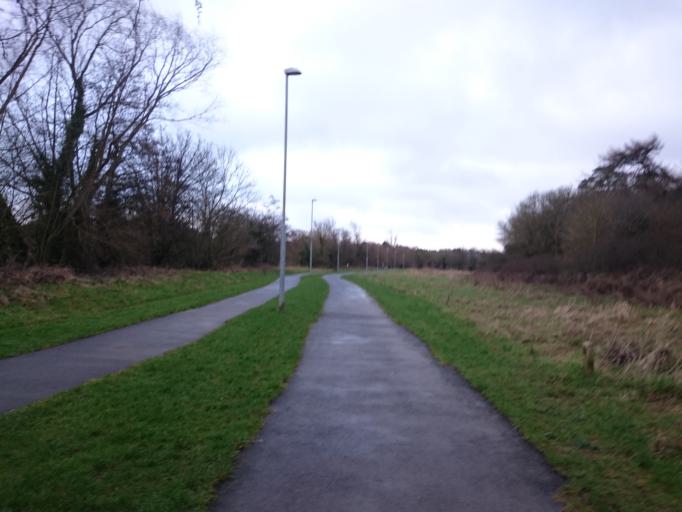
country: IE
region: Leinster
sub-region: Kilkenny
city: Kilkenny
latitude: 52.6674
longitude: -7.2593
